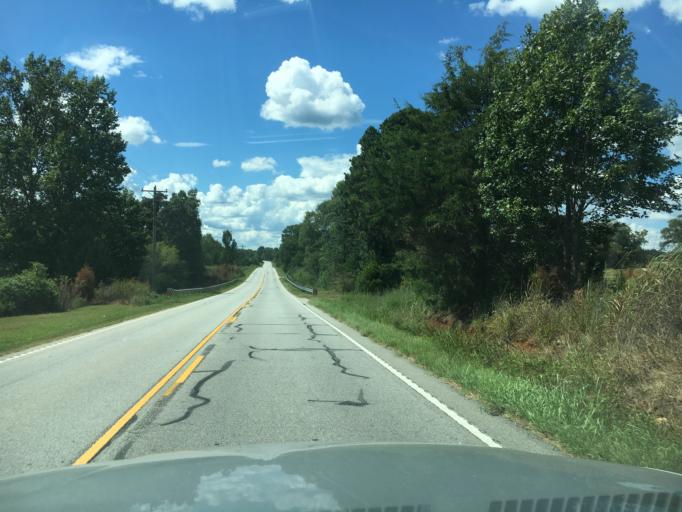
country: US
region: South Carolina
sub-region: Greenwood County
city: Ware Shoals
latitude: 34.5206
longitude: -82.1715
